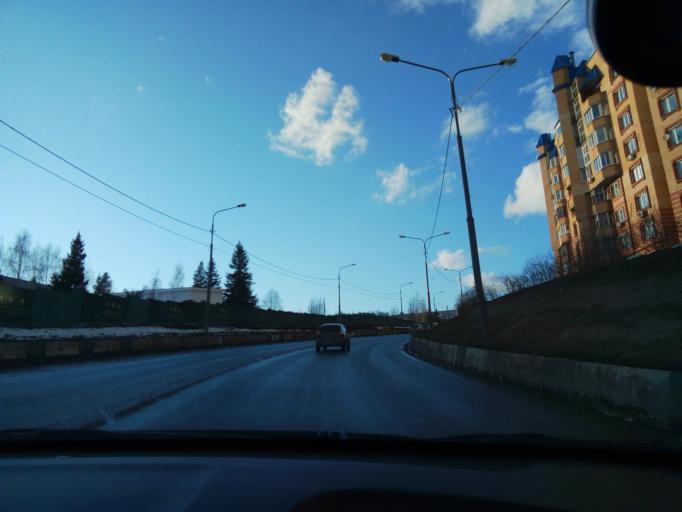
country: RU
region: Chuvashia
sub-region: Cheboksarskiy Rayon
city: Cheboksary
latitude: 56.1400
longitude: 47.2274
